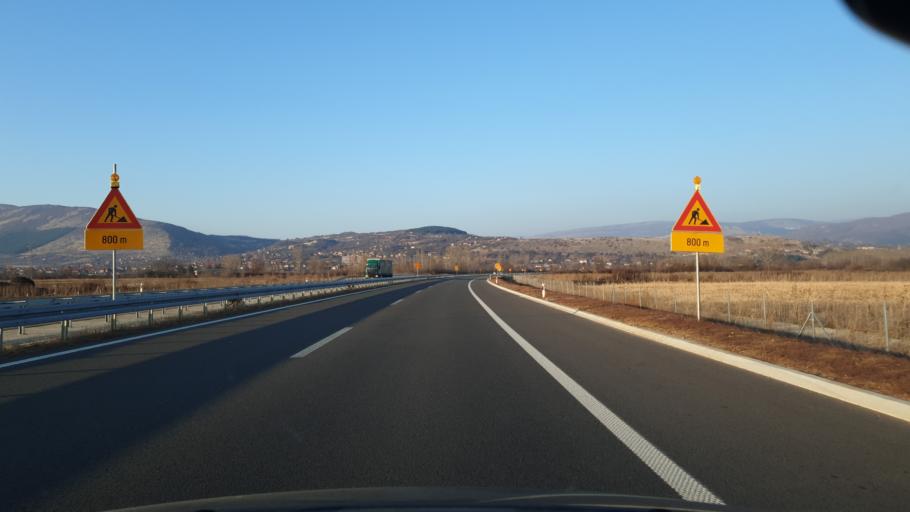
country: RS
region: Central Serbia
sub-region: Pirotski Okrug
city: Pirot
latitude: 43.1437
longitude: 22.5676
